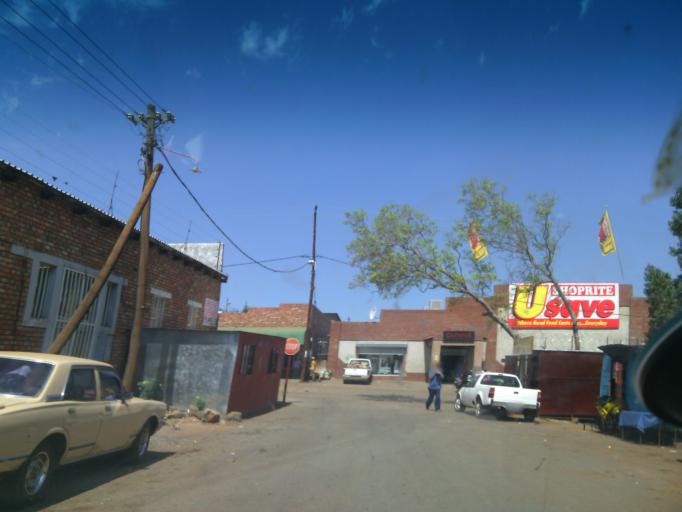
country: ZA
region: Northern Cape
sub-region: Frances Baard District Municipality
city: Barkly West
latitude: -28.5381
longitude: 24.5171
